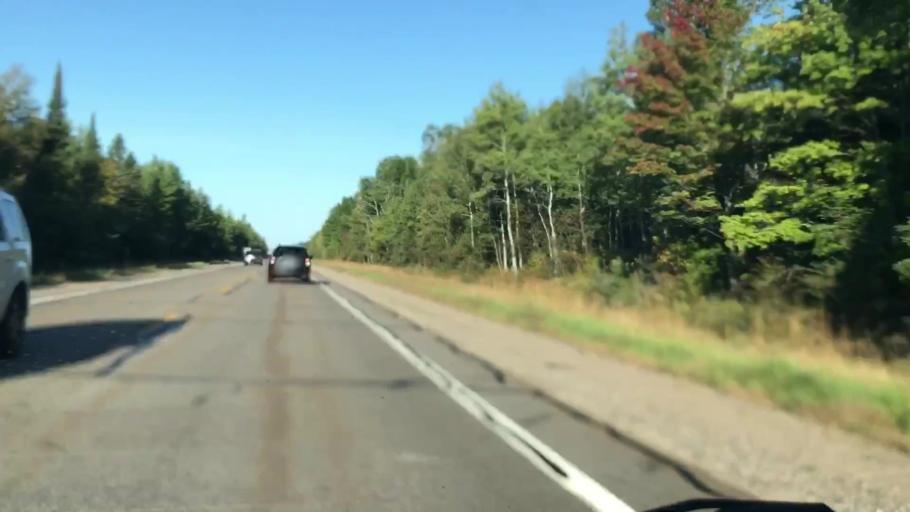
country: US
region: Michigan
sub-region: Chippewa County
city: Sault Ste. Marie
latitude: 46.3756
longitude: -84.6233
